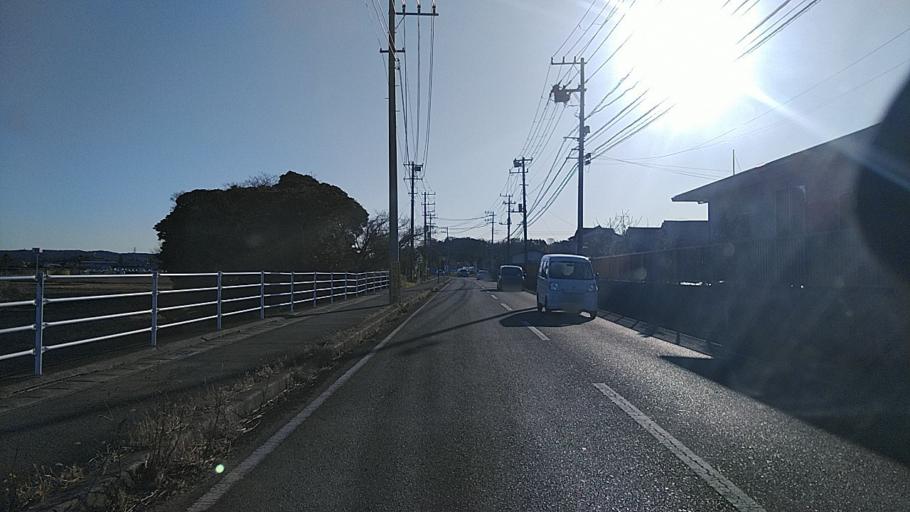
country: JP
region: Chiba
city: Kimitsu
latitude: 35.3202
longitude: 139.8846
